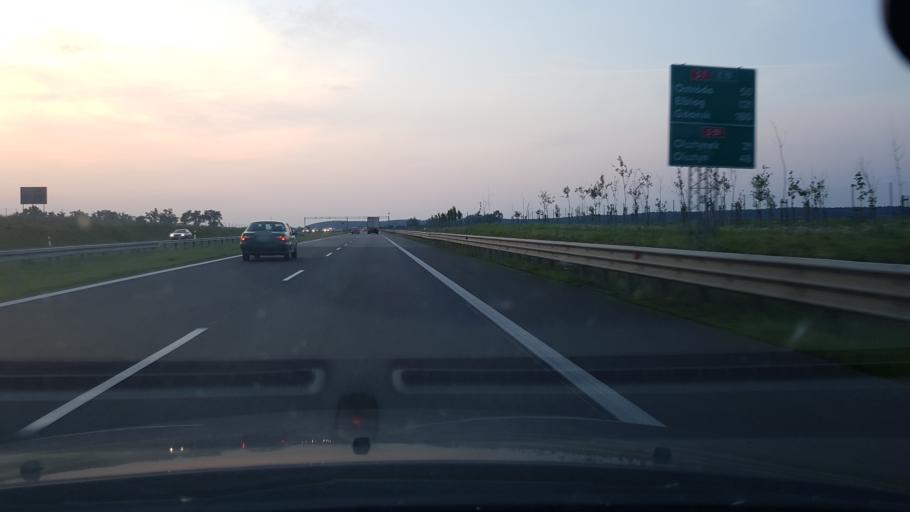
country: PL
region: Warmian-Masurian Voivodeship
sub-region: Powiat nidzicki
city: Nidzica
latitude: 53.3901
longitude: 20.3683
